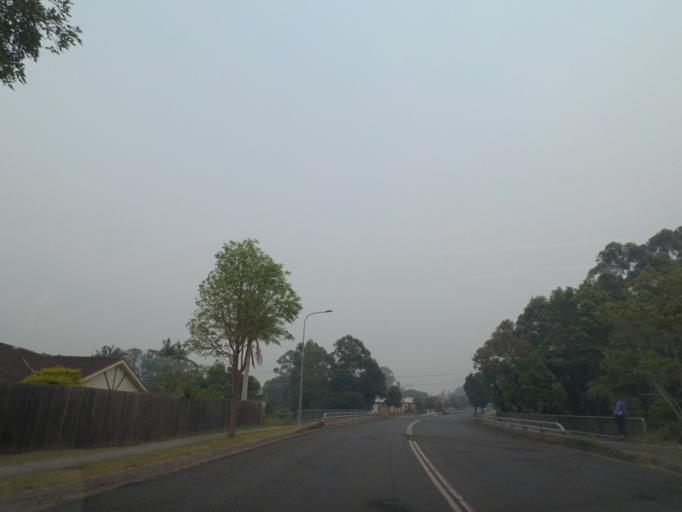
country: AU
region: New South Wales
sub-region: Coffs Harbour
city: Coffs Harbour
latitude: -30.2942
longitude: 153.1101
